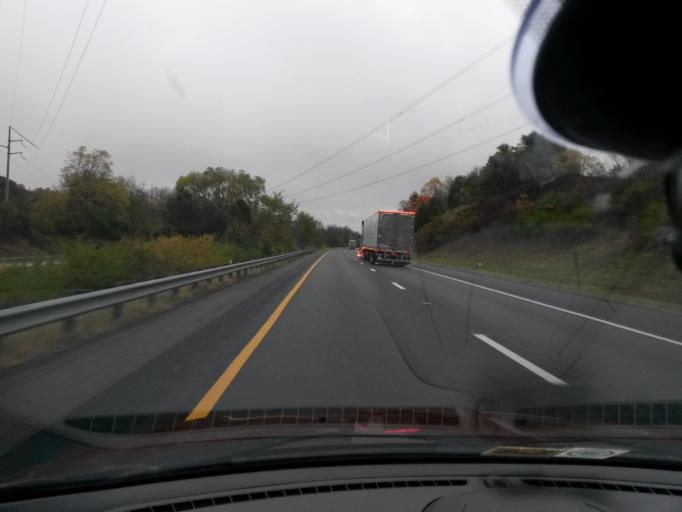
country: US
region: Virginia
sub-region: Botetourt County
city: Daleville
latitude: 37.4017
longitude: -79.8970
